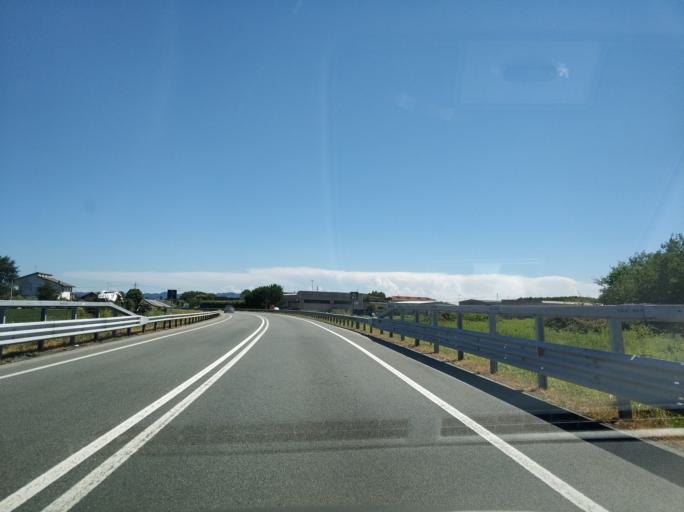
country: IT
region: Piedmont
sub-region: Provincia di Torino
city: Rondissone
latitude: 45.2470
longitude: 7.9566
